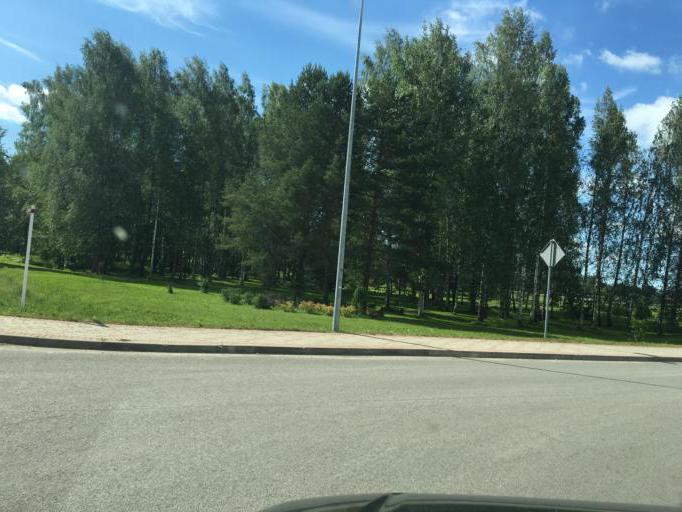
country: LV
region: Balvu Rajons
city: Balvi
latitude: 57.1386
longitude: 27.2585
